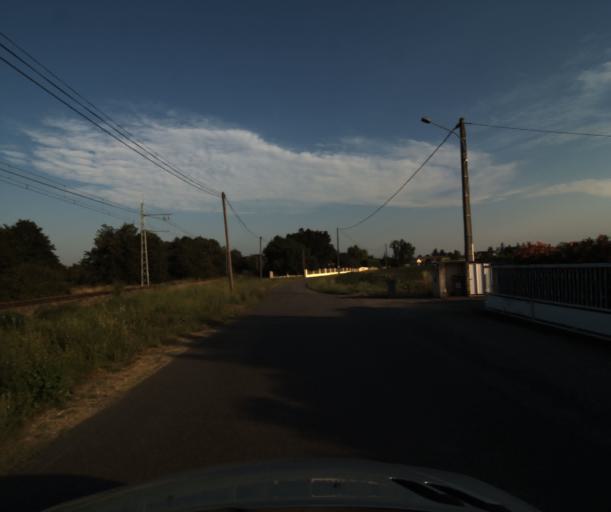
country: FR
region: Midi-Pyrenees
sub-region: Departement de la Haute-Garonne
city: Lacroix-Falgarde
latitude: 43.4851
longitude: 1.3965
